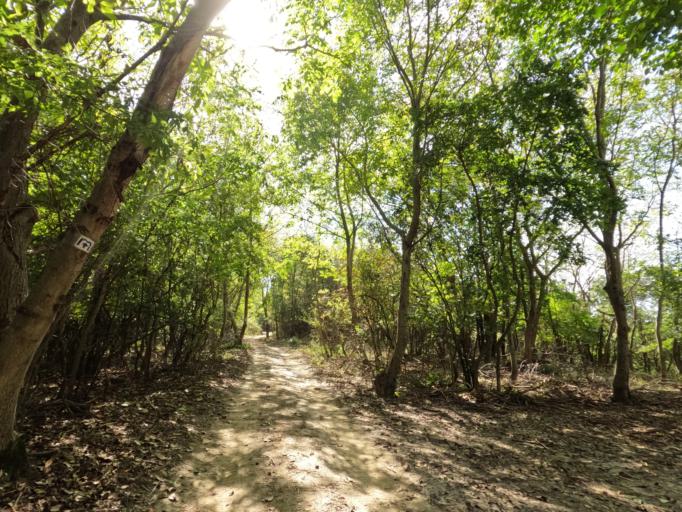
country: HU
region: Tolna
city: Szentgalpuszta
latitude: 46.3349
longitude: 18.6463
